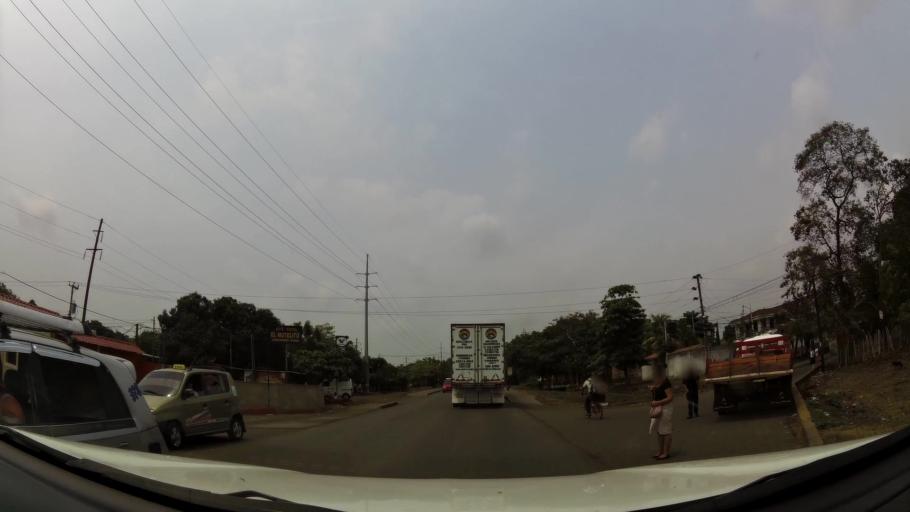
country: NI
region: Chinandega
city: Chinandega
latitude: 12.6484
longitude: -87.1263
